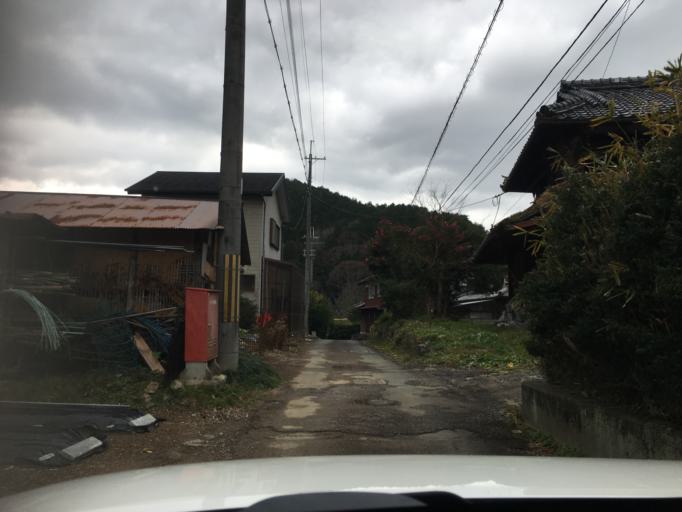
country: JP
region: Kyoto
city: Kameoka
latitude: 35.0400
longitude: 135.4760
